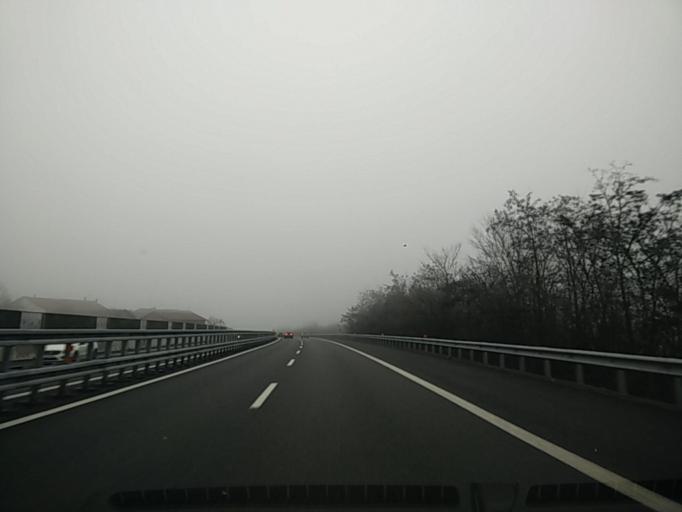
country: IT
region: Piedmont
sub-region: Provincia di Asti
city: Castello di Annone
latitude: 44.9086
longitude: 8.3157
